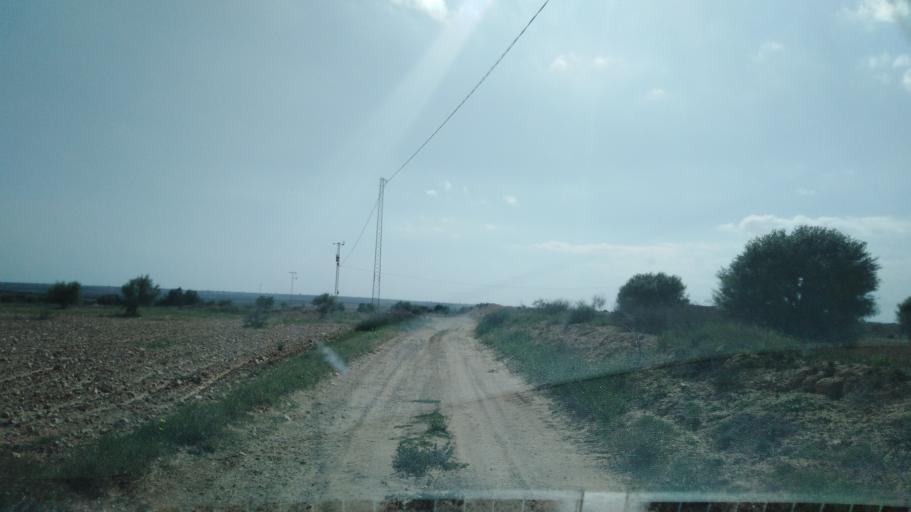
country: TN
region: Safaqis
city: Bi'r `Ali Bin Khalifah
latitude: 34.7961
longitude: 10.3742
